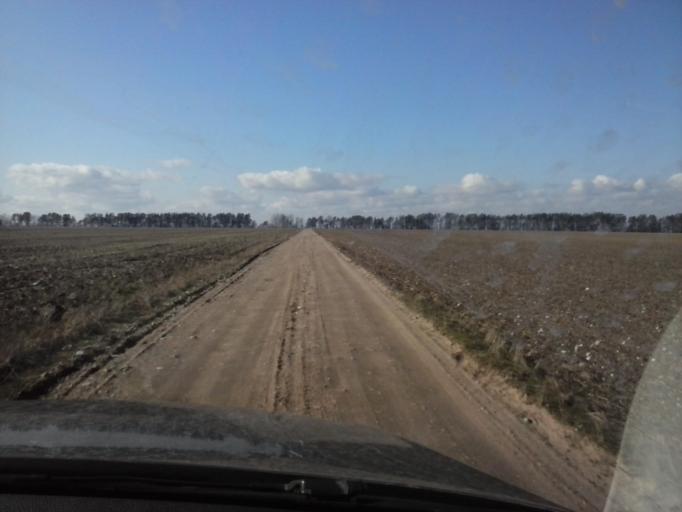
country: EE
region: Tartu
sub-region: Puhja vald
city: Puhja
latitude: 58.2849
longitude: 26.1543
